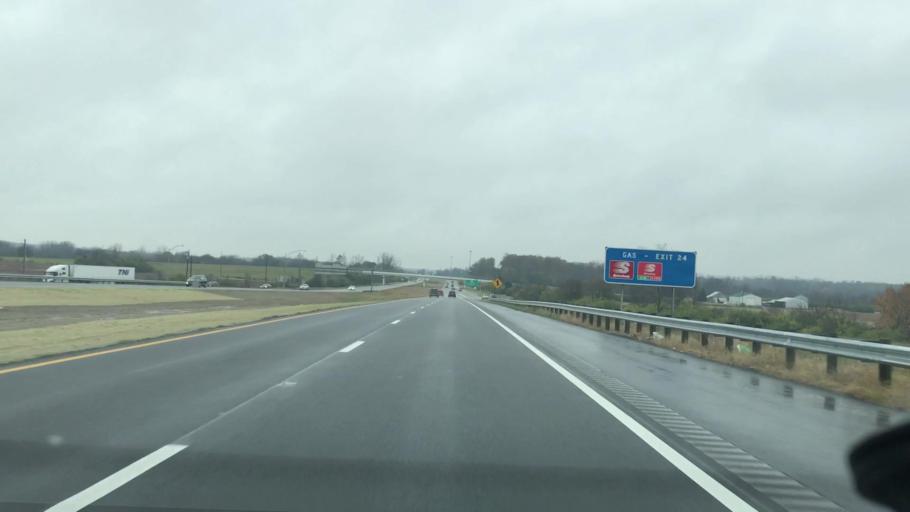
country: US
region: Ohio
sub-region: Clark County
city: Holiday Valley
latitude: 39.8633
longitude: -83.9941
